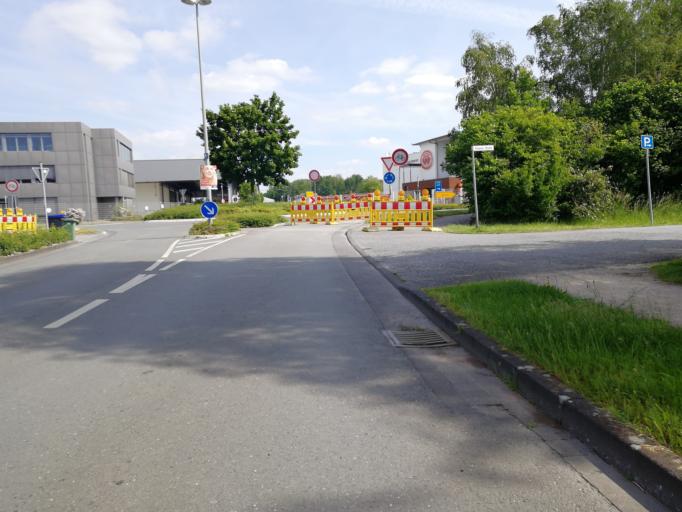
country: DE
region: North Rhine-Westphalia
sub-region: Regierungsbezirk Detmold
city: Verl
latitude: 51.8943
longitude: 8.4628
